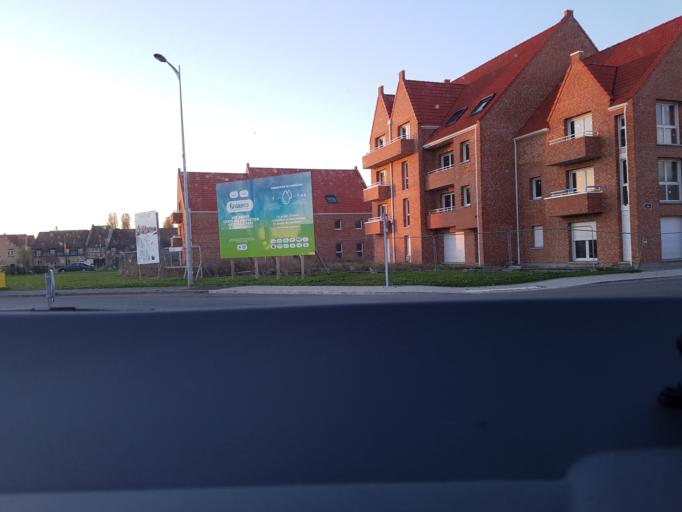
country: FR
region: Nord-Pas-de-Calais
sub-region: Departement du Nord
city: Cappelle-la-Grande
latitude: 50.9985
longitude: 2.3736
